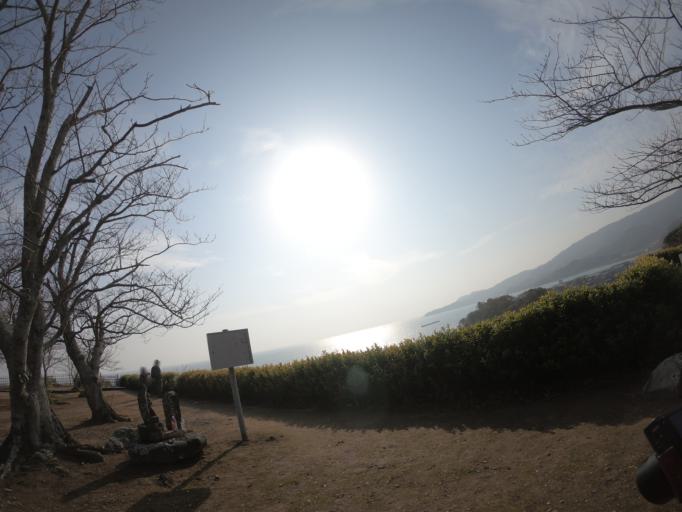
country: JP
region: Kumamoto
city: Hondo
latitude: 32.6289
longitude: 130.2540
